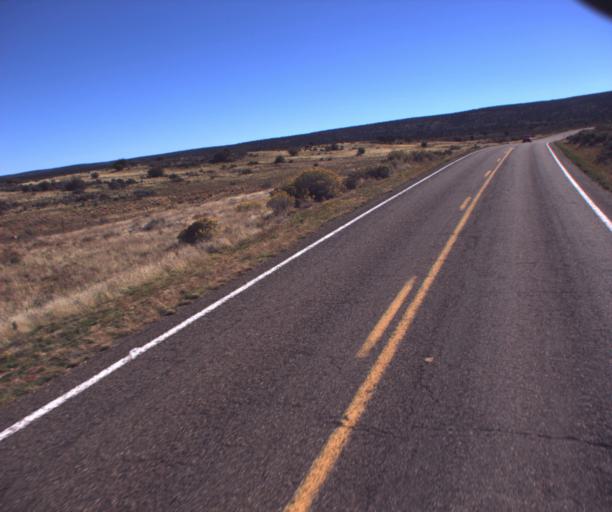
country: US
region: Arizona
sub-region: Coconino County
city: Fredonia
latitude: 36.8520
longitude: -112.2916
